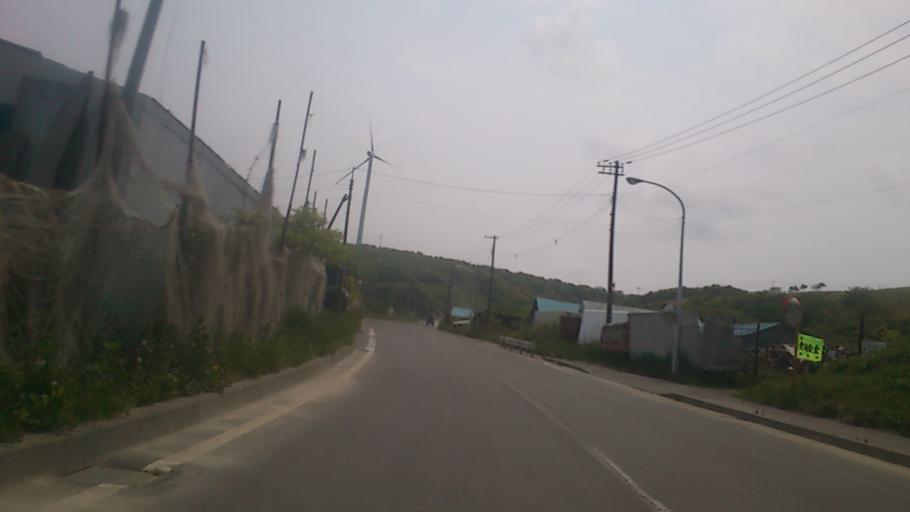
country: JP
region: Hokkaido
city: Nemuro
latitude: 43.2817
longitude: 145.5645
